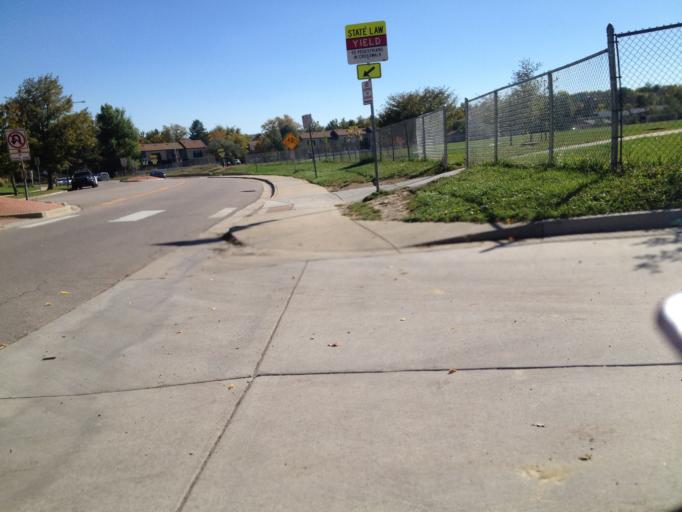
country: US
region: Colorado
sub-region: Boulder County
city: Boulder
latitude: 39.9839
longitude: -105.2395
